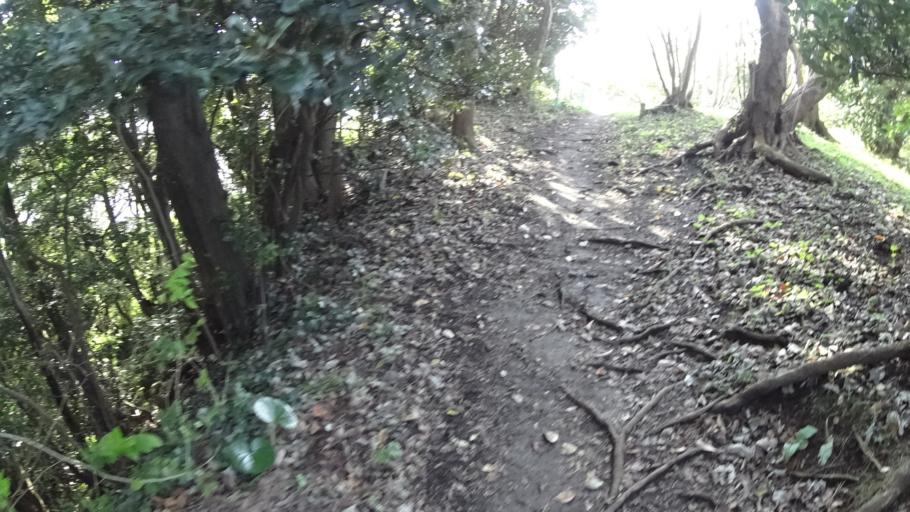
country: JP
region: Kanagawa
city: Hayama
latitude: 35.2723
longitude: 139.5908
